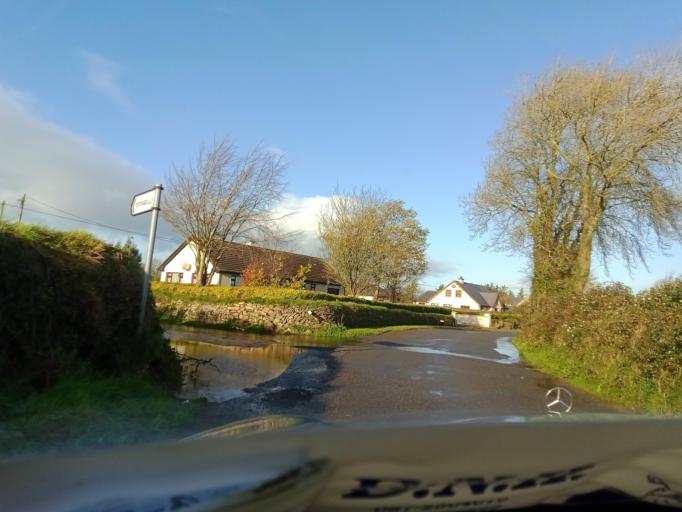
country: IE
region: Leinster
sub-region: Kilkenny
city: Mooncoin
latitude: 52.2751
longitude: -7.2353
